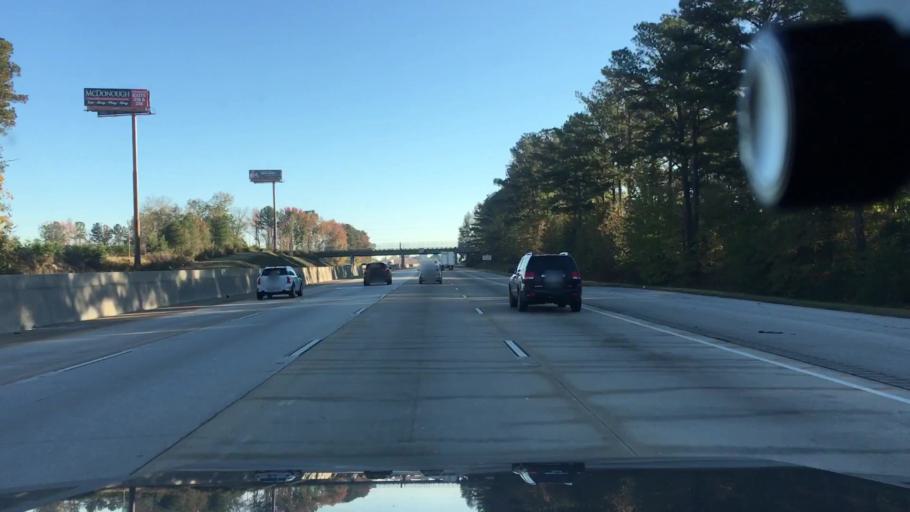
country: US
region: Georgia
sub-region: Fulton County
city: Fairburn
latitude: 33.5371
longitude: -84.5945
